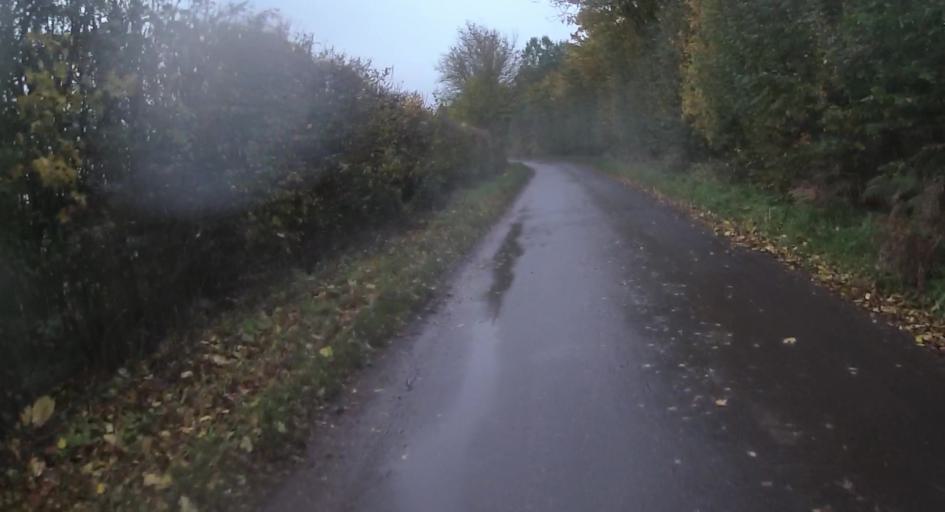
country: GB
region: England
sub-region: Hampshire
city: Four Marks
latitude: 51.1319
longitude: -1.0941
